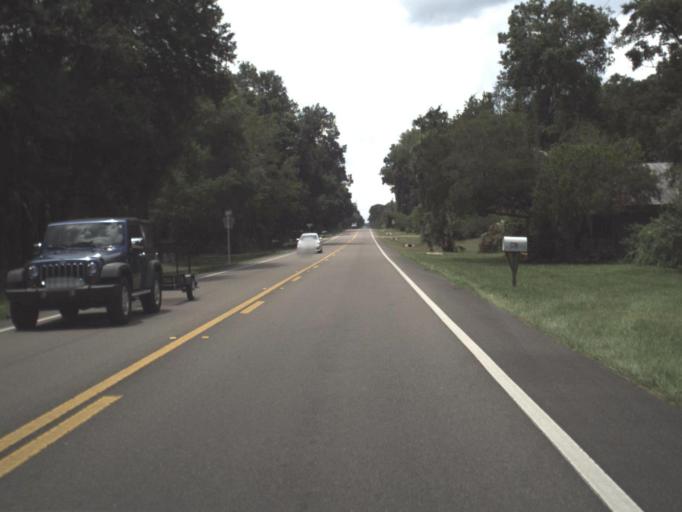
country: US
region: Florida
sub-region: Levy County
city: Williston
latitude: 29.4426
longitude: -82.4668
